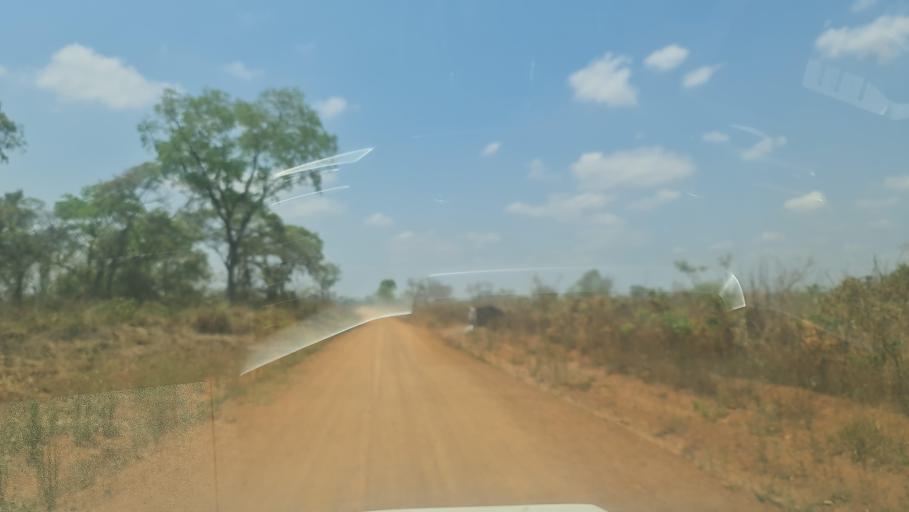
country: MW
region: Southern Region
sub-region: Nsanje District
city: Nsanje
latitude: -17.4058
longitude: 35.8082
